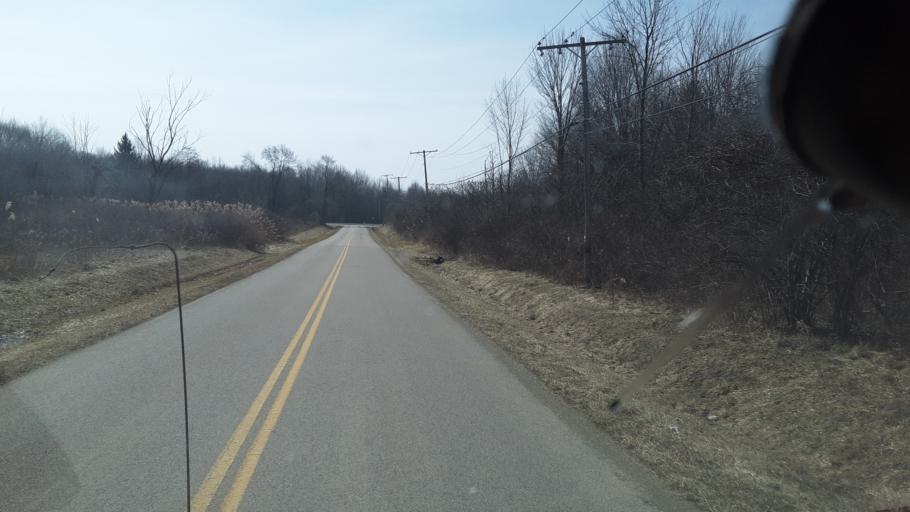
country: US
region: Ohio
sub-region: Ashtabula County
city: Jefferson
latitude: 41.7487
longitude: -80.7415
